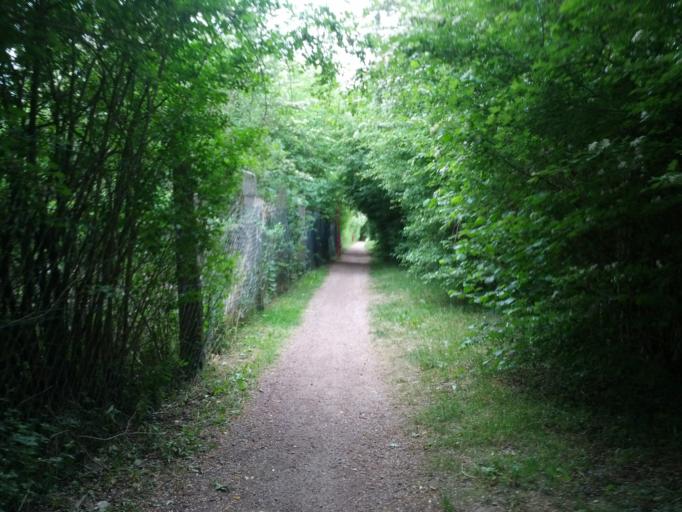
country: DE
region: Thuringia
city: Eisenach
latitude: 50.9932
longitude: 10.2980
